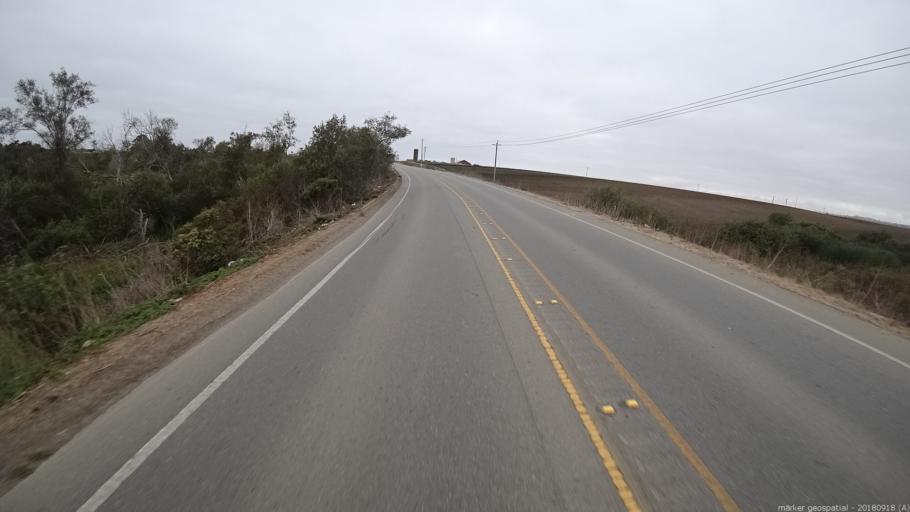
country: US
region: California
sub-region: Monterey County
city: Prunedale
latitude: 36.7462
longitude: -121.6962
